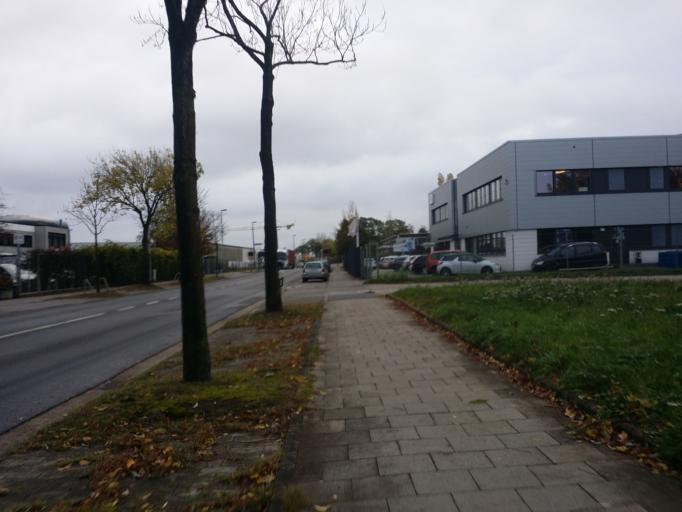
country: DE
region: Lower Saxony
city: Delmenhorst
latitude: 53.0230
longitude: 8.6397
